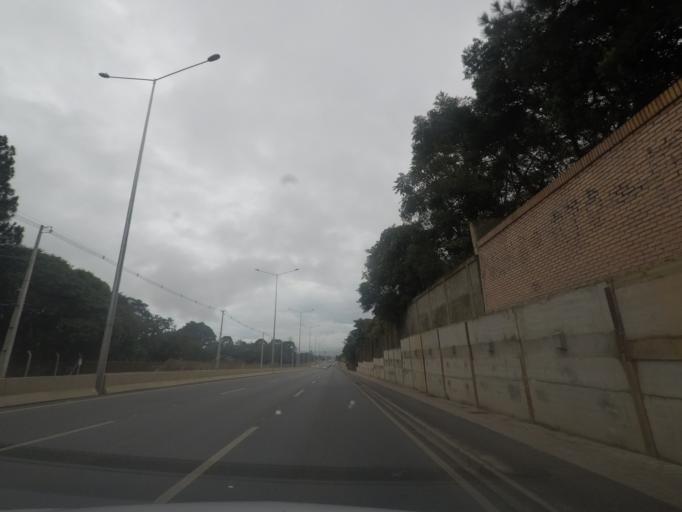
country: BR
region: Parana
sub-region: Piraquara
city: Piraquara
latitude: -25.4548
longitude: -49.1112
